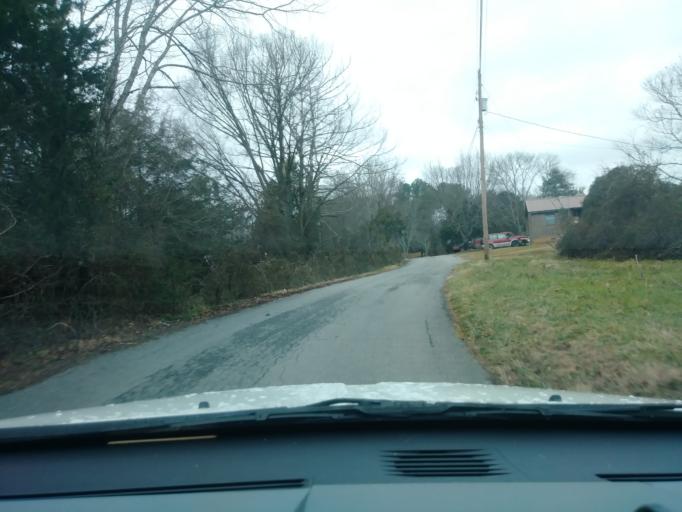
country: US
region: Tennessee
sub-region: Greene County
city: Greeneville
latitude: 36.1001
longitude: -82.8835
